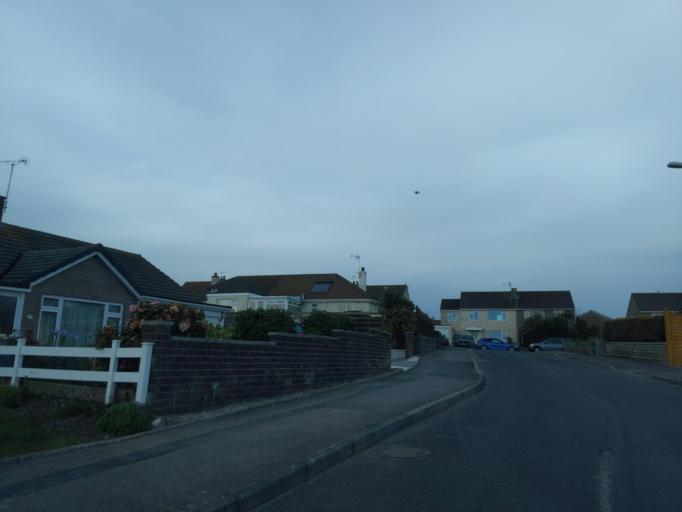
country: GB
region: England
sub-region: Cornwall
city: Torpoint
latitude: 50.3761
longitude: -4.2048
